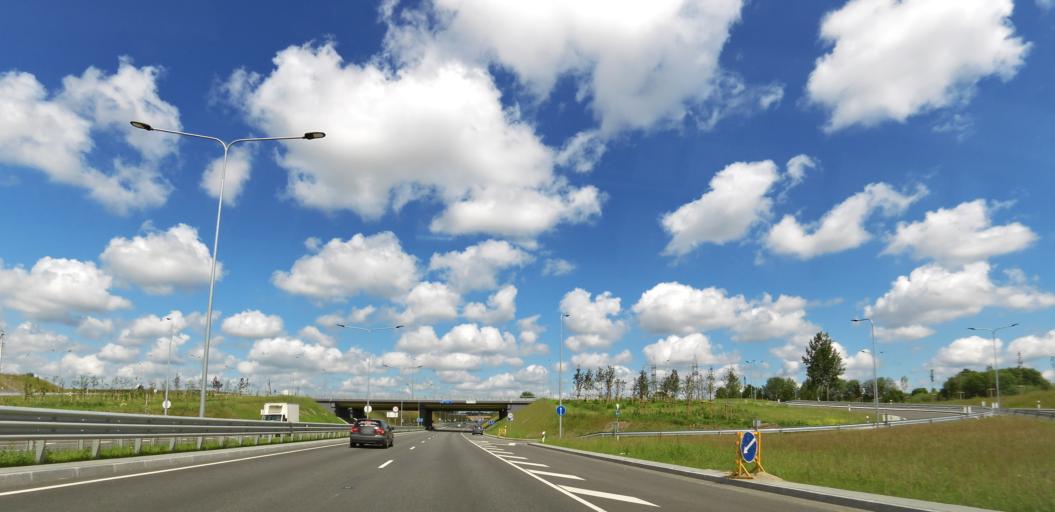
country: LT
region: Vilnius County
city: Justiniskes
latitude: 54.7233
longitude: 25.2081
